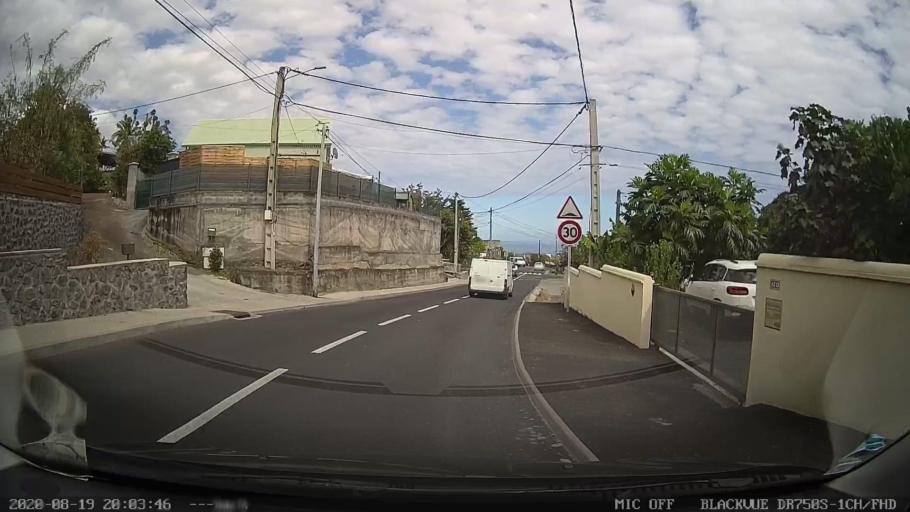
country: RE
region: Reunion
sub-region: Reunion
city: La Possession
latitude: -20.9512
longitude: 55.3444
